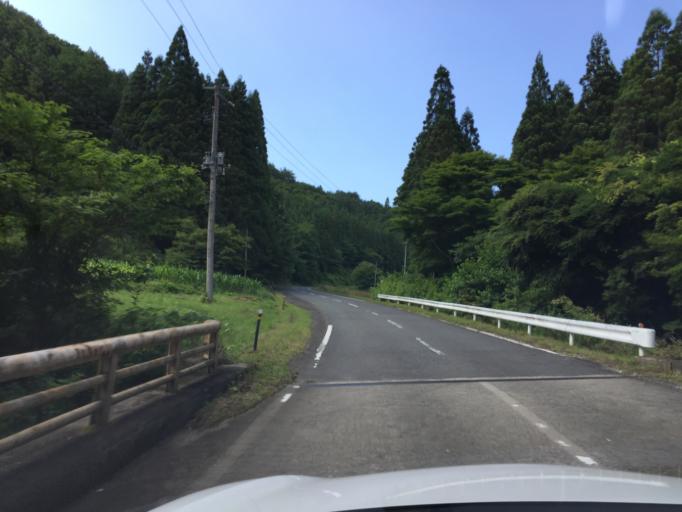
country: JP
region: Fukushima
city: Ishikawa
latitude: 37.1273
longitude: 140.6417
